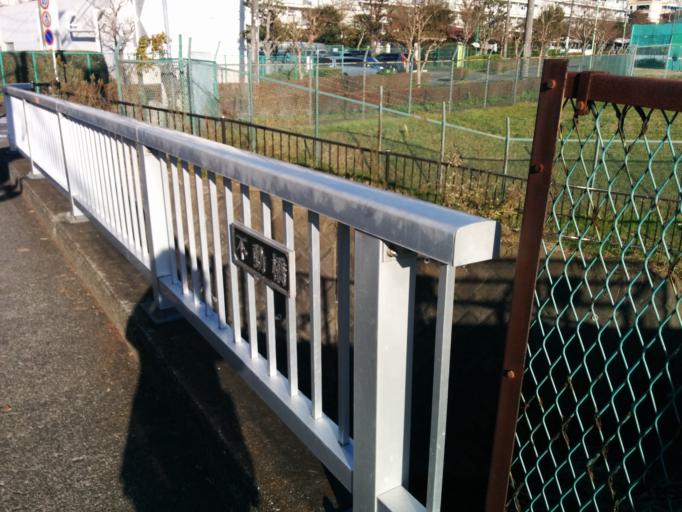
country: JP
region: Kanagawa
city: Fujisawa
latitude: 35.3711
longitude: 139.4387
